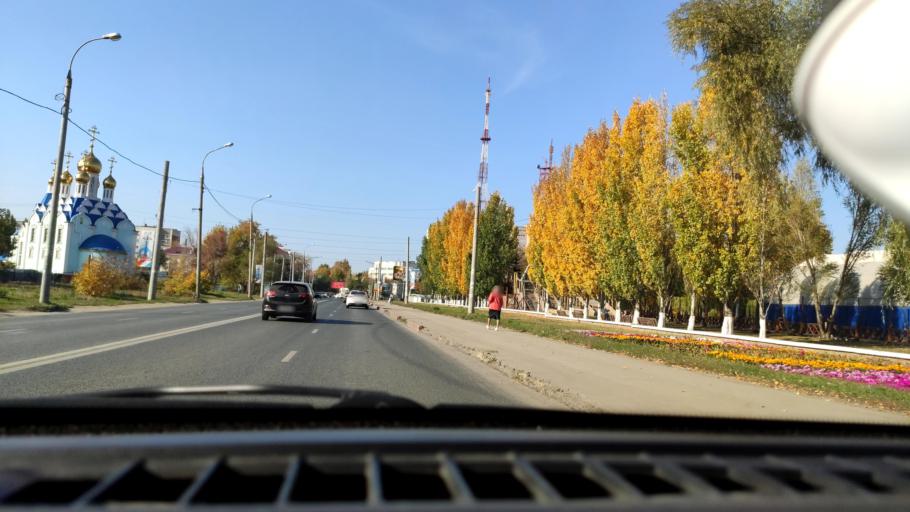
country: RU
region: Samara
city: Samara
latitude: 53.2263
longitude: 50.1968
